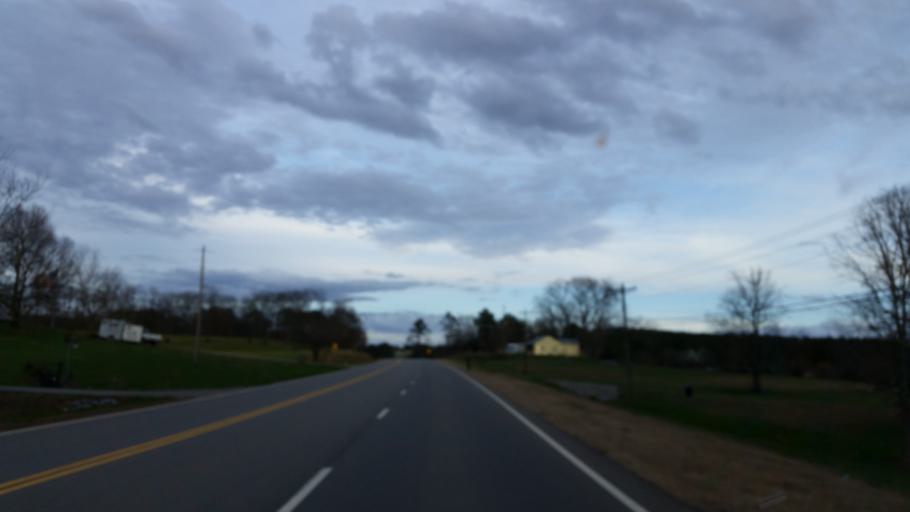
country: US
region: Georgia
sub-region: Bartow County
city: Rydal
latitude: 34.4483
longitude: -84.7824
